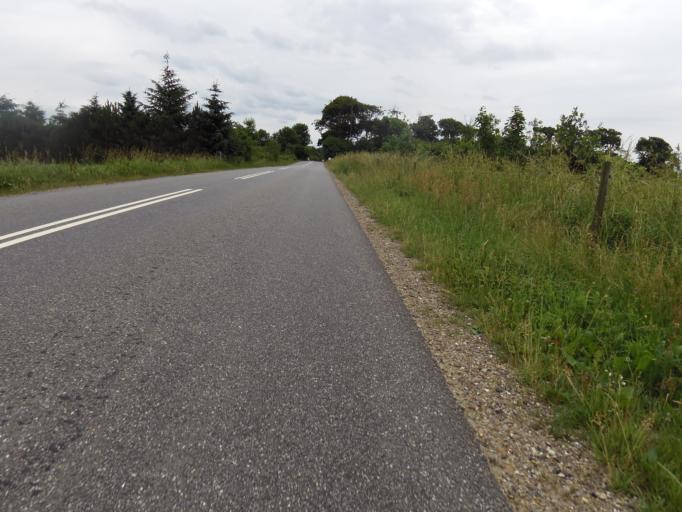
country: DK
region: Central Jutland
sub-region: Holstebro Kommune
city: Vinderup
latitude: 56.4119
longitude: 8.7093
